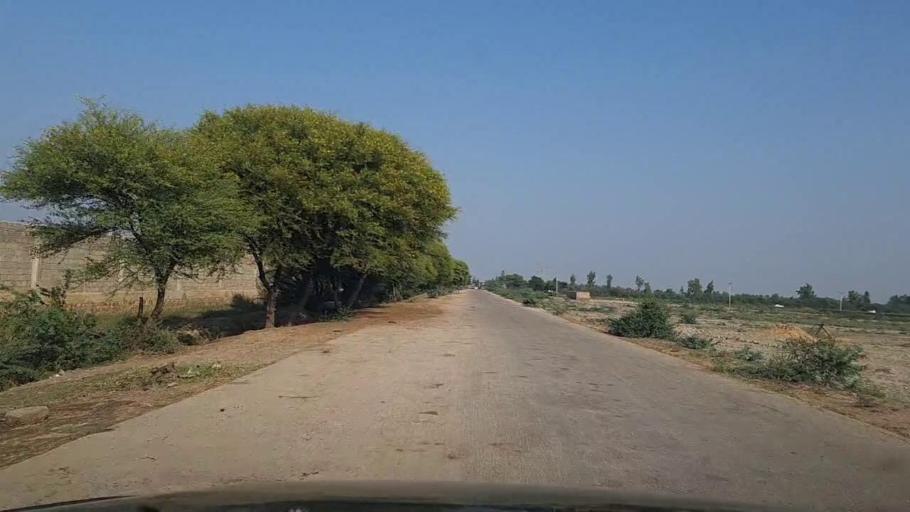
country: PK
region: Sindh
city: Chuhar Jamali
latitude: 24.5884
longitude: 68.0821
